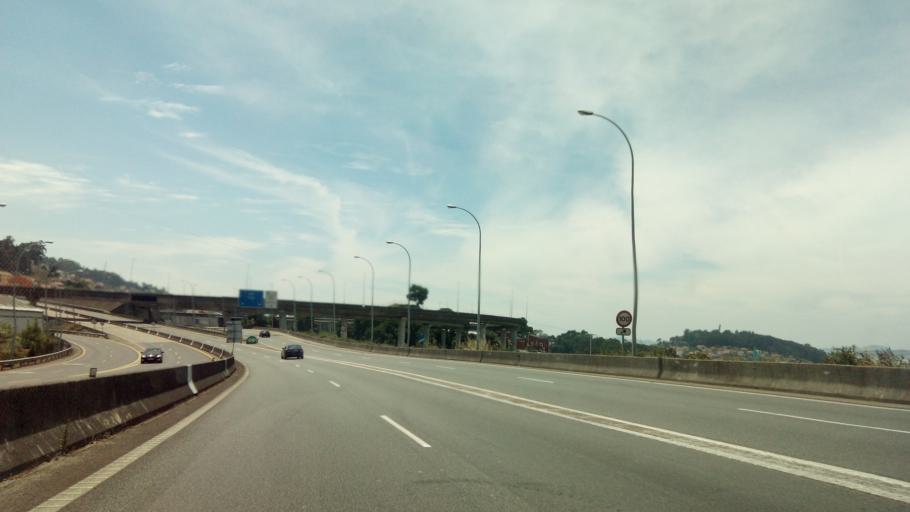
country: ES
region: Galicia
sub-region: Provincia de Pontevedra
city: Vigo
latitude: 42.2610
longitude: -8.6730
